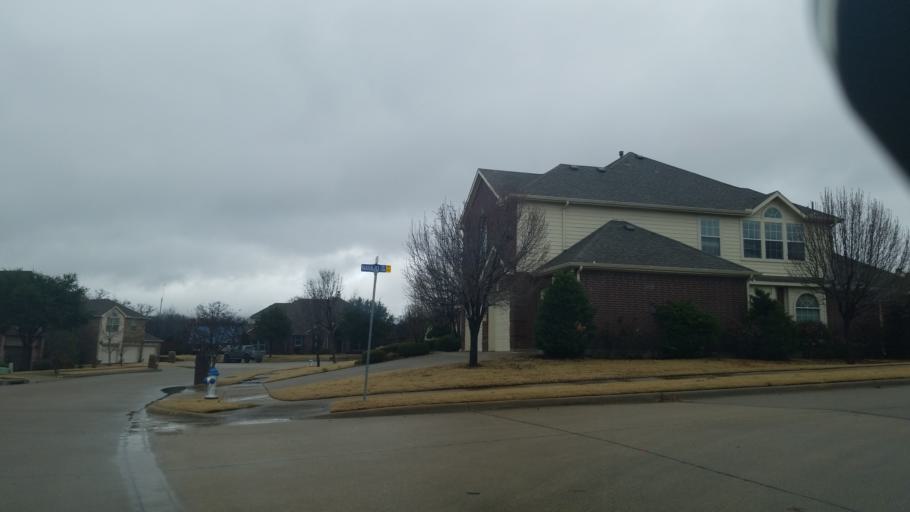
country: US
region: Texas
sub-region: Denton County
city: Corinth
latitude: 33.1410
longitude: -97.0917
